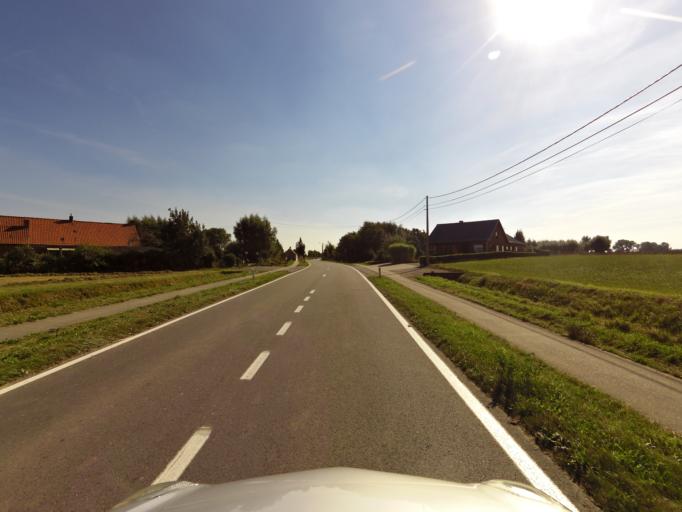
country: BE
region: Flanders
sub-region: Provincie West-Vlaanderen
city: Poperinge
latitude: 50.9111
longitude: 2.7391
